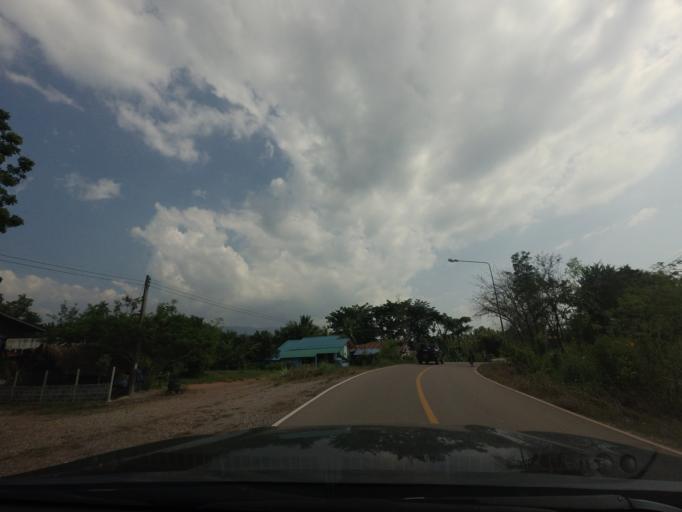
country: TH
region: Phitsanulok
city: Nakhon Thai
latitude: 17.0421
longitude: 100.9140
